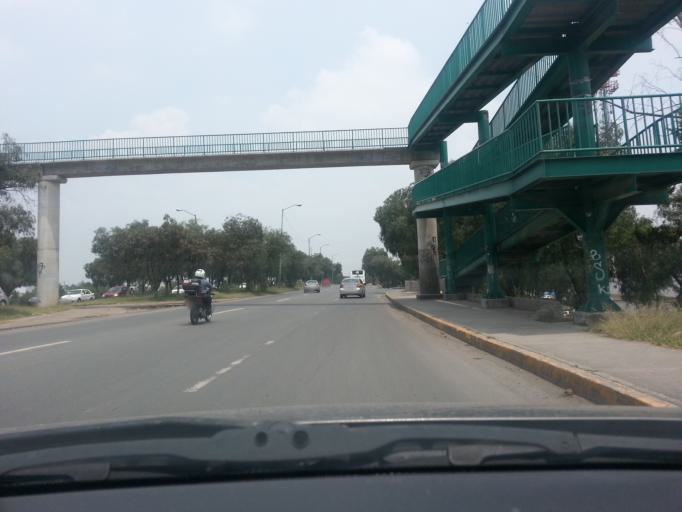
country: MX
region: Mexico
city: Cuautitlan Izcalli
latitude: 19.6702
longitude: -99.2111
